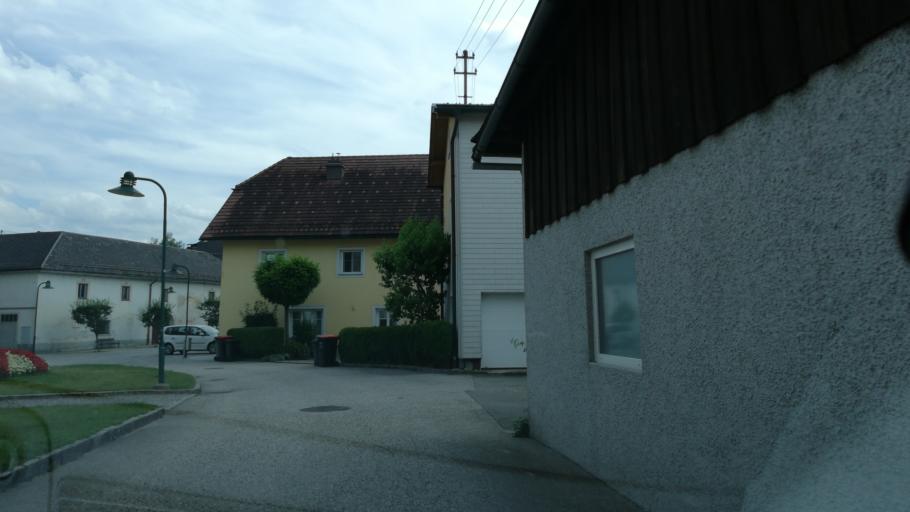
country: AT
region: Upper Austria
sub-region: Politischer Bezirk Vocklabruck
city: Attnang-Puchheim
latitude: 47.9918
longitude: 13.6880
